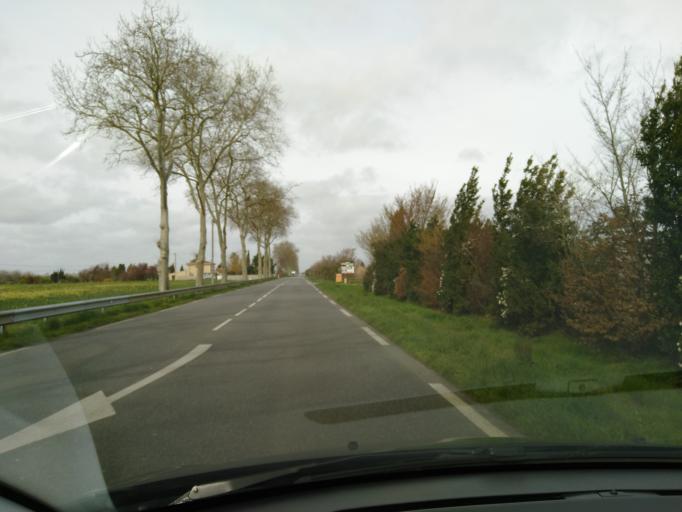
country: FR
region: Midi-Pyrenees
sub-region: Departement de la Haute-Garonne
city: Seilh
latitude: 43.7088
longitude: 1.3408
